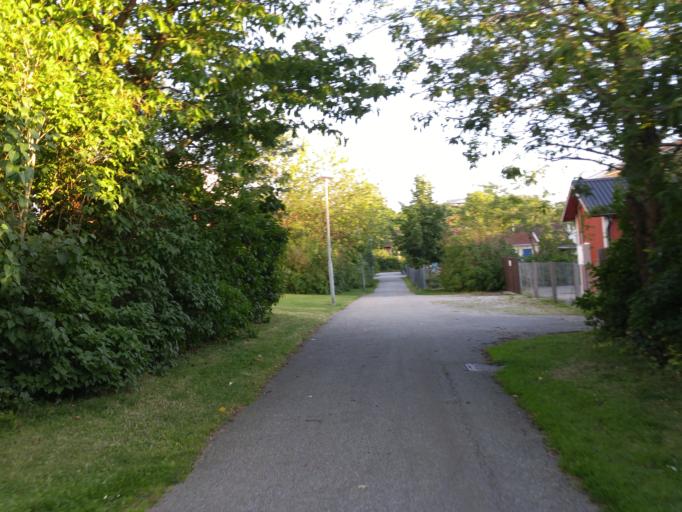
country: SE
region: Skane
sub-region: Lunds Kommun
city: Lund
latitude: 55.7188
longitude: 13.2000
